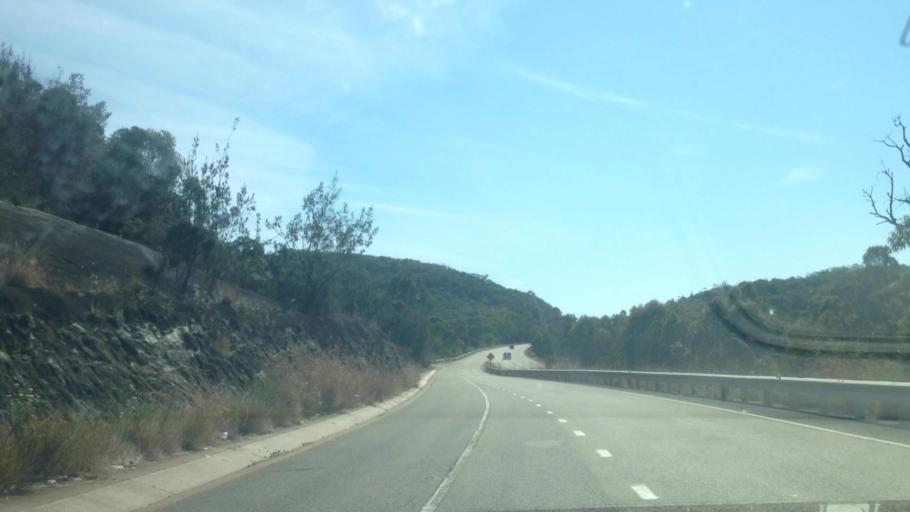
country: AU
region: New South Wales
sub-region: Lake Macquarie Shire
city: Toronto
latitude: -32.9862
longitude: 151.5194
